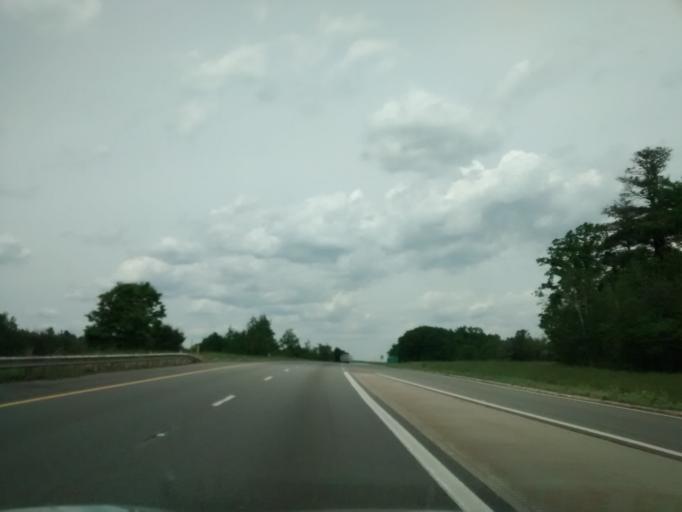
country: US
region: Massachusetts
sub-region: Worcester County
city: East Douglas
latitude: 42.1050
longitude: -71.7050
